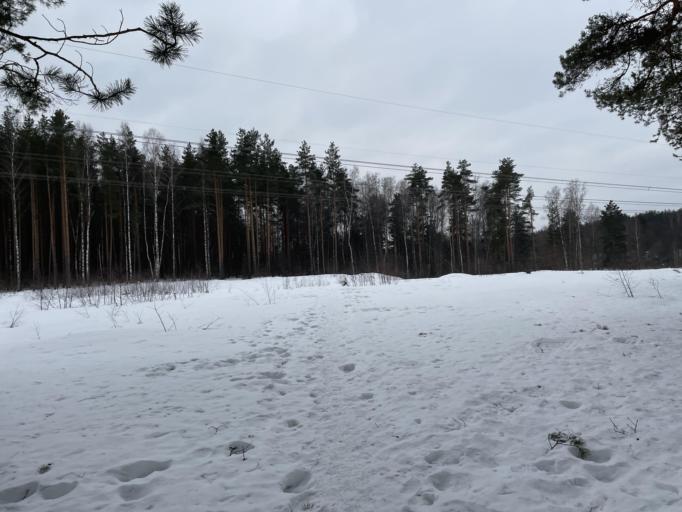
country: RU
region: Vladimir
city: Pokrov
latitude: 55.9412
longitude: 39.2373
